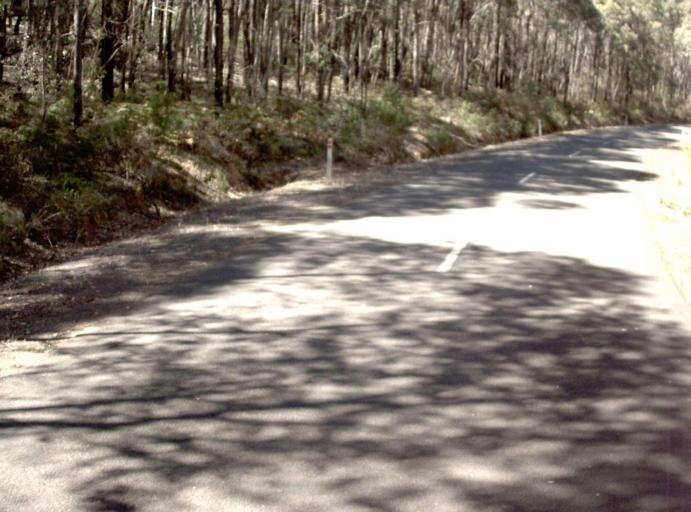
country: AU
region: New South Wales
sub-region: Bombala
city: Bombala
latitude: -37.0918
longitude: 148.7664
